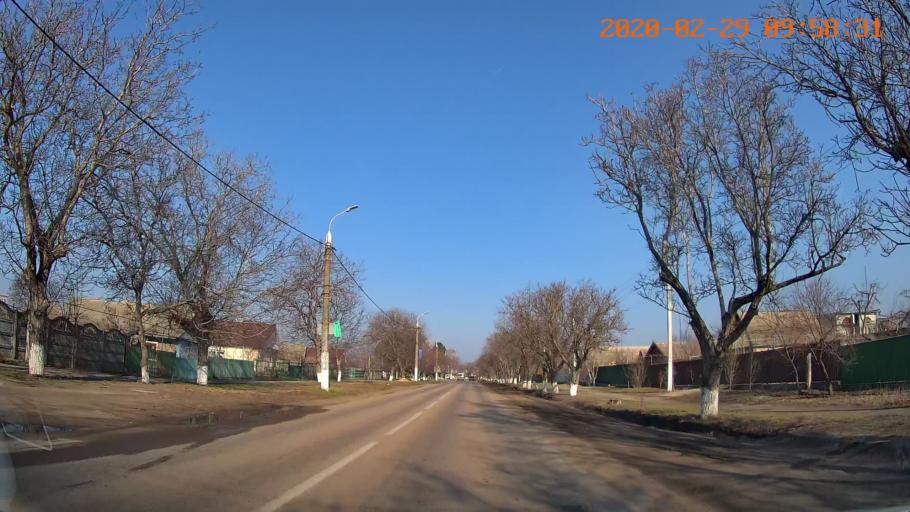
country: MD
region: Telenesti
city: Slobozia
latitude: 46.7495
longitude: 29.6911
